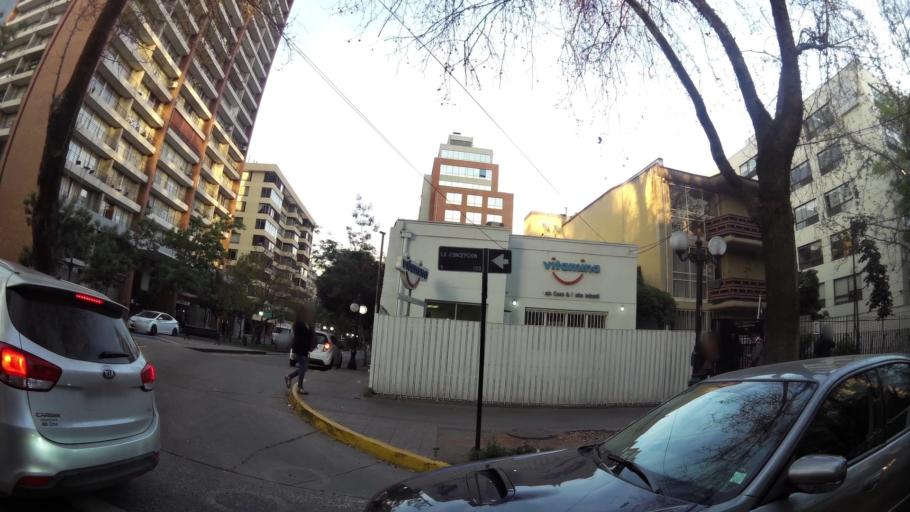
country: CL
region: Santiago Metropolitan
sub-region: Provincia de Santiago
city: Santiago
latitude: -33.4245
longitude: -70.6161
